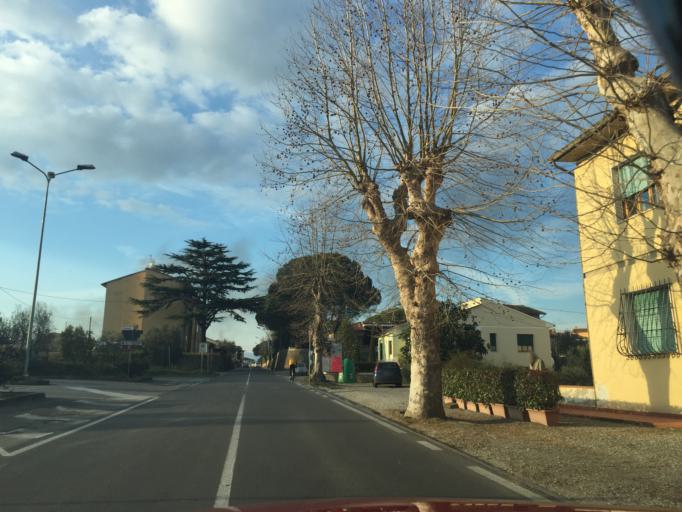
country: IT
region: Tuscany
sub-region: Provincia di Pistoia
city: Lamporecchio
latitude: 43.8208
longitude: 10.8815
